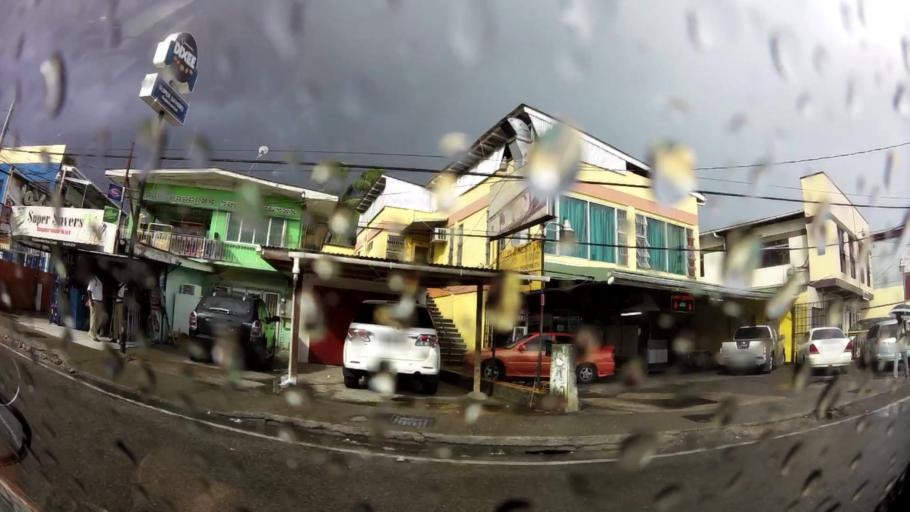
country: TT
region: Tunapuna/Piarco
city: Tunapuna
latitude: 10.6497
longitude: -61.4087
